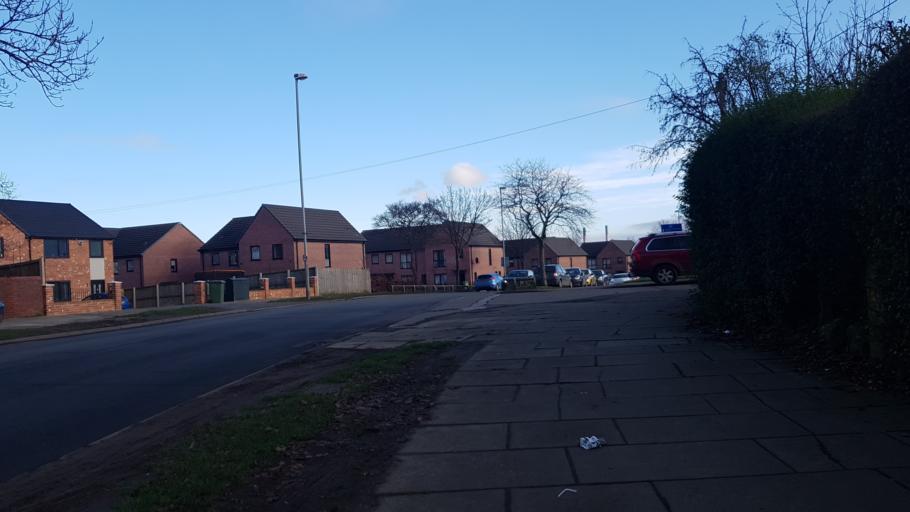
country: GB
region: England
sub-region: City and Borough of Wakefield
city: Pontefract
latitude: 53.7247
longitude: -1.3175
